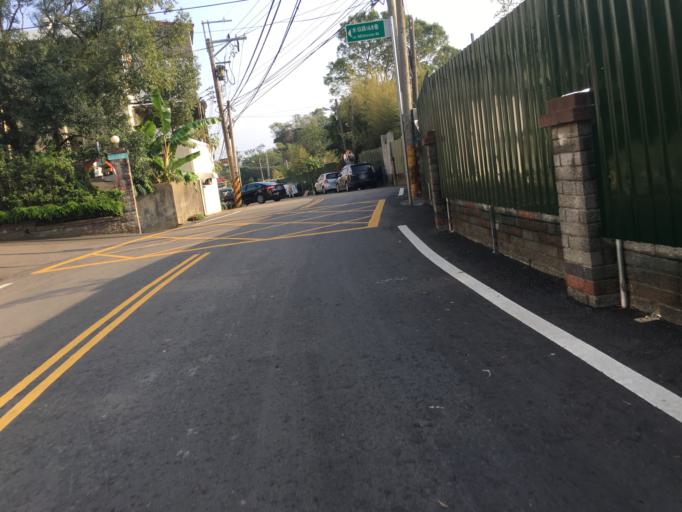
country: TW
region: Taiwan
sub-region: Hsinchu
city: Hsinchu
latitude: 24.7477
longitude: 121.0369
